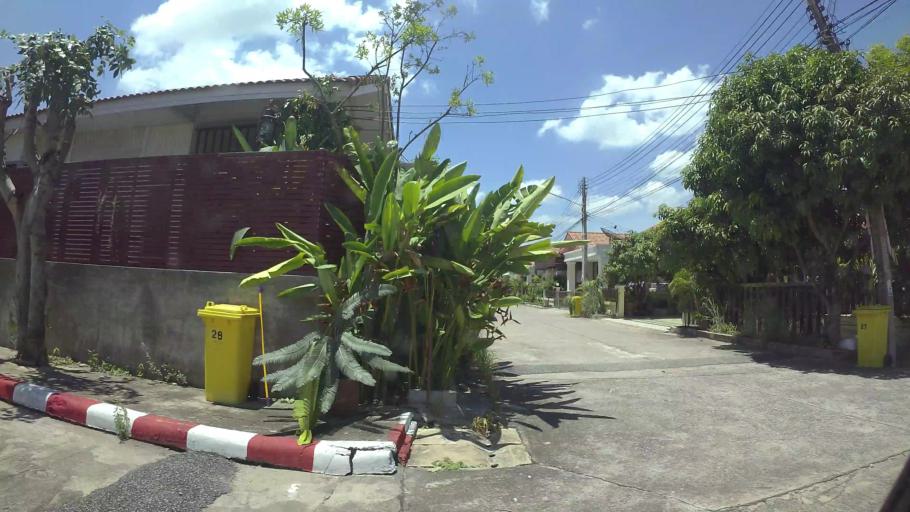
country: TH
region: Chon Buri
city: Si Racha
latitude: 13.1282
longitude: 100.9460
